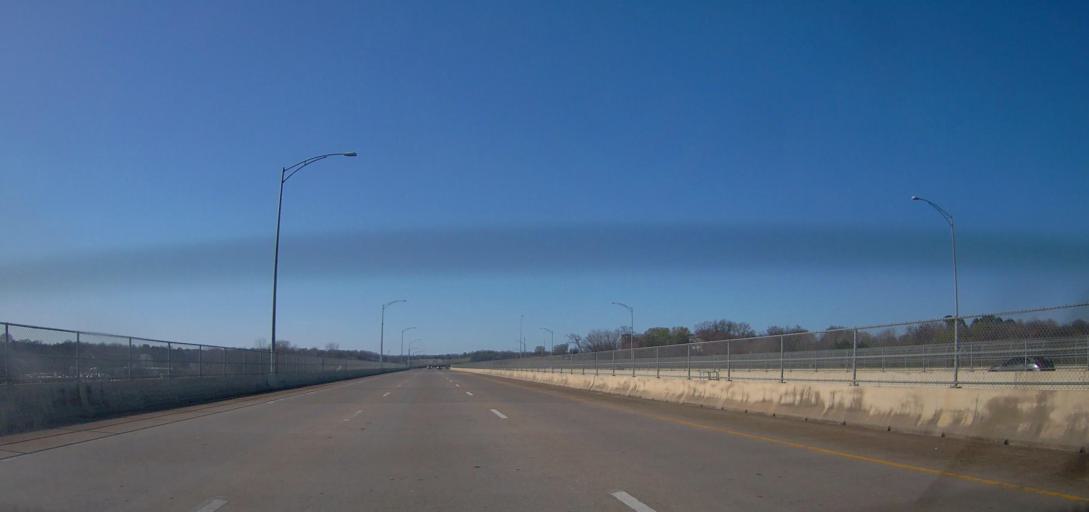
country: US
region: Alabama
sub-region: Lauderdale County
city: East Florence
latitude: 34.7985
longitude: -87.6488
